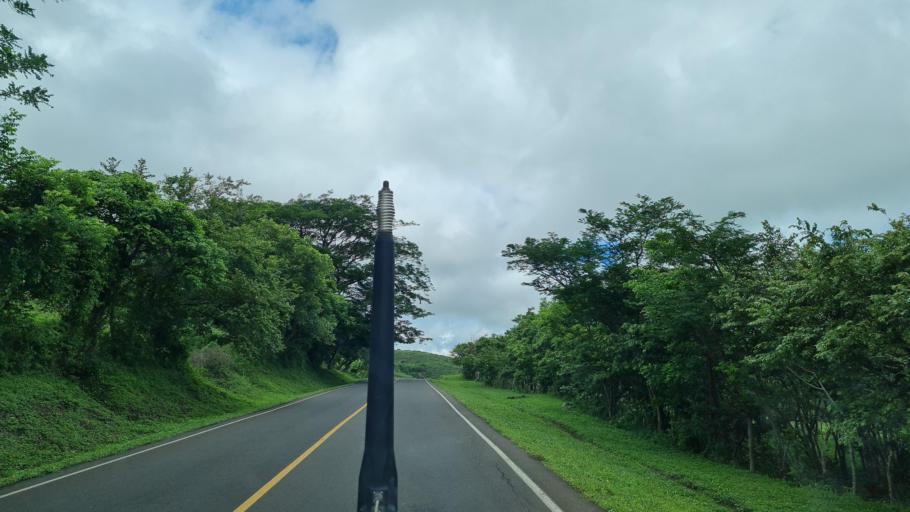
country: NI
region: Matagalpa
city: Terrabona
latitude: 12.5956
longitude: -85.9323
